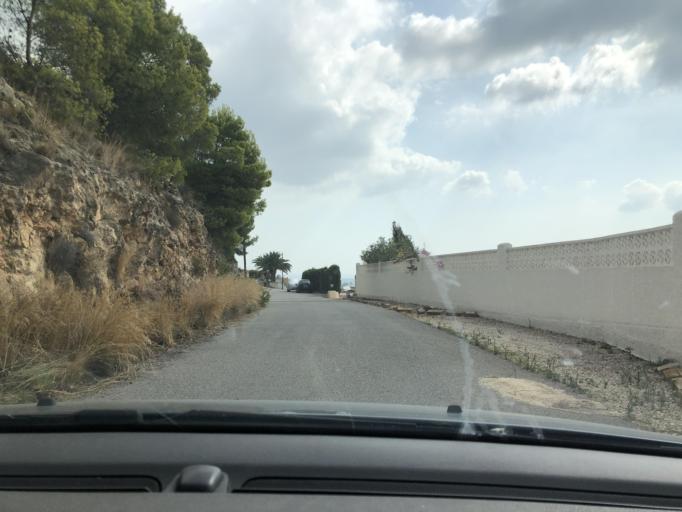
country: ES
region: Valencia
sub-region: Provincia de Alicante
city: Callosa d'En Sarria
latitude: 38.6326
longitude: -0.1106
